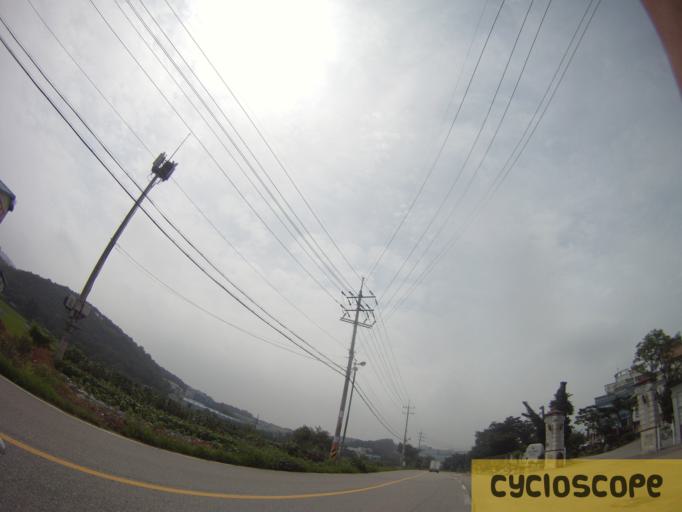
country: KR
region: Gyeonggi-do
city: Hwaseong-si
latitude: 37.1633
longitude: 126.9201
